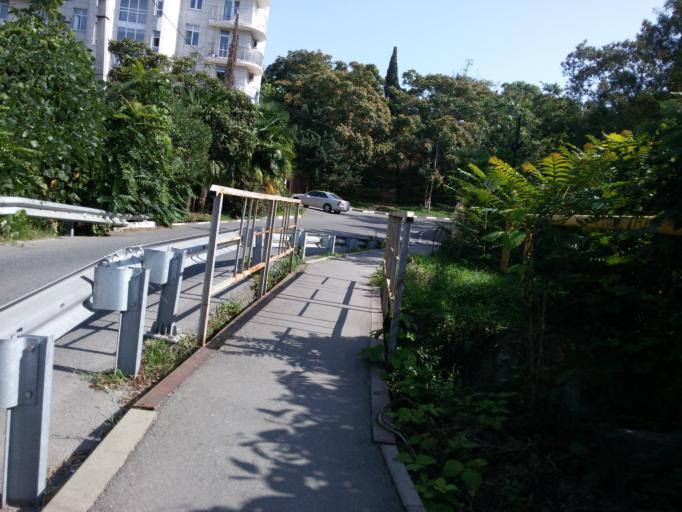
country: RU
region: Krasnodarskiy
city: Adler
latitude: 43.4189
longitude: 39.9366
